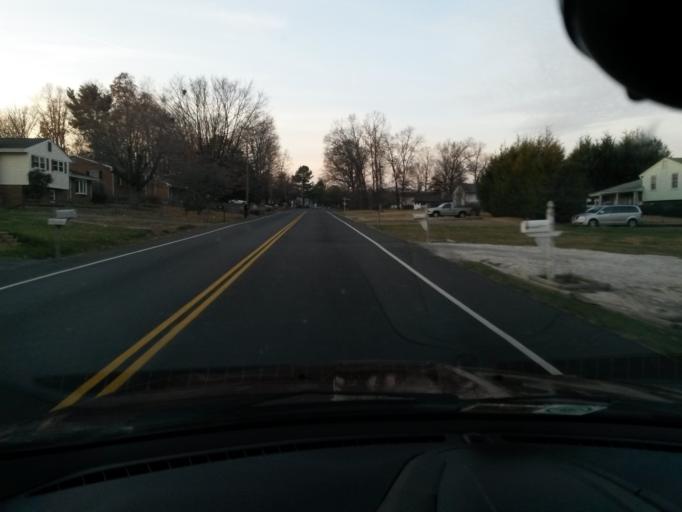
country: US
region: Virginia
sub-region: Roanoke County
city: Hollins
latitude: 37.3336
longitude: -79.9393
